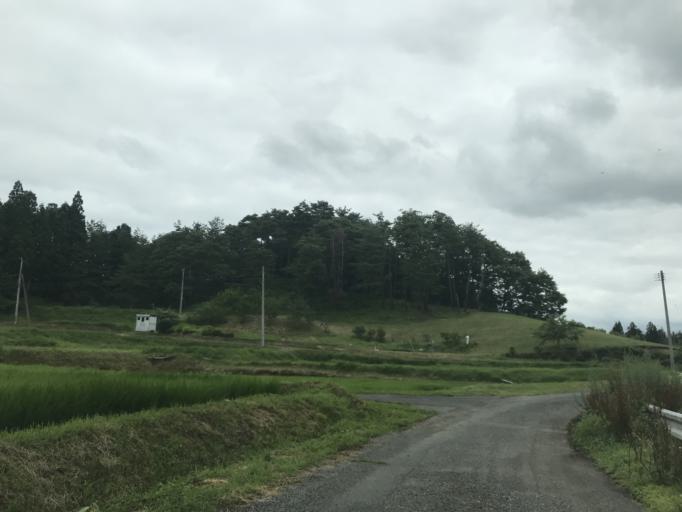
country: JP
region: Iwate
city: Ichinoseki
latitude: 38.9077
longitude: 141.0720
